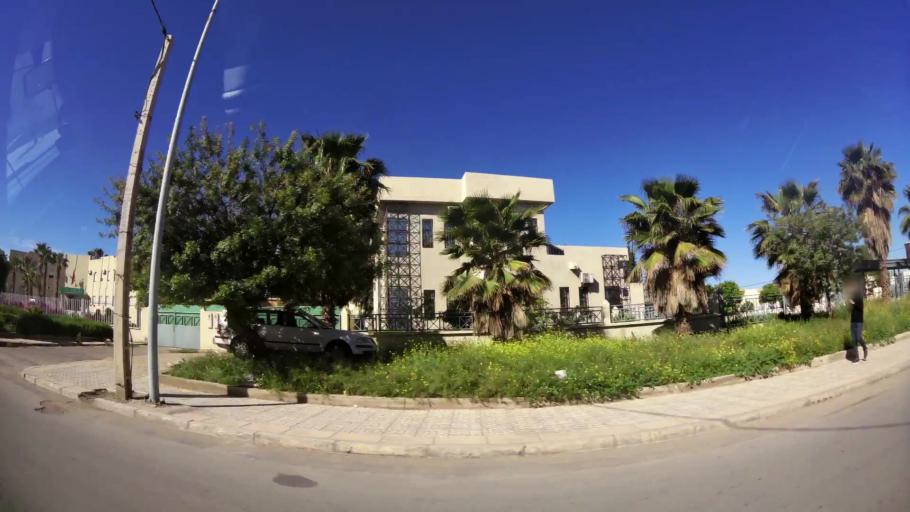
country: MA
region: Oriental
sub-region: Oujda-Angad
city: Oujda
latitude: 34.6523
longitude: -1.8965
